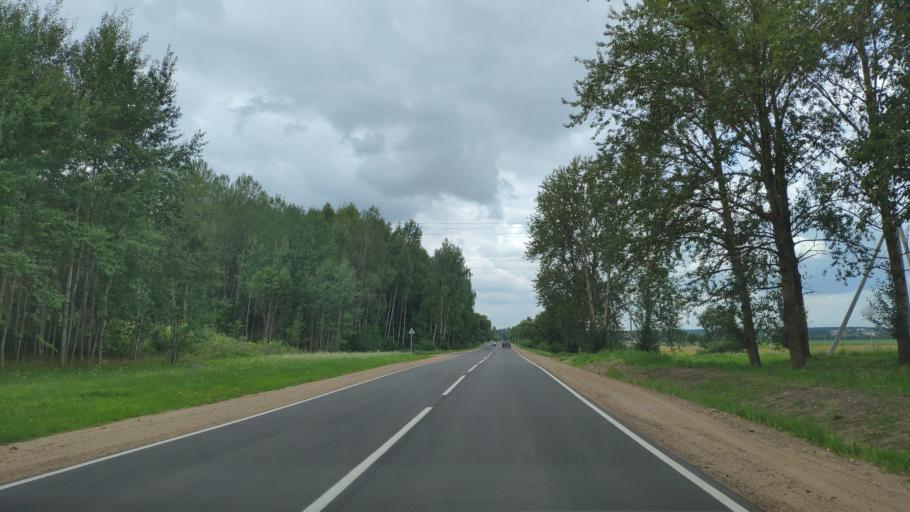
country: BY
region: Minsk
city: Syomkava
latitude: 53.9938
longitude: 27.4685
